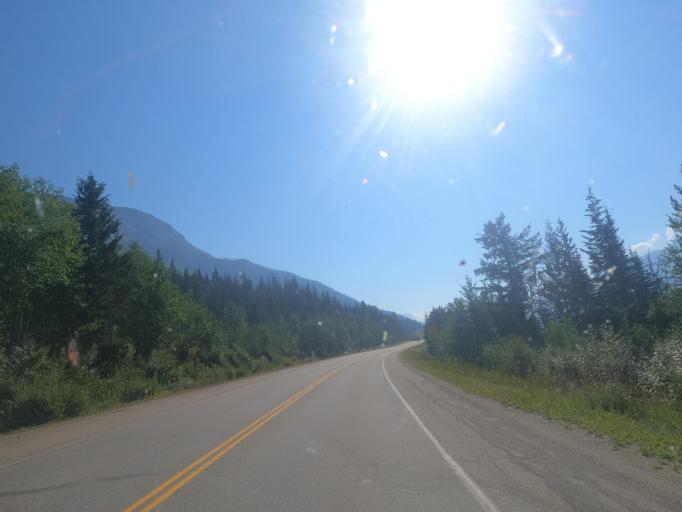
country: CA
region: Alberta
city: Jasper Park Lodge
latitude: 52.9719
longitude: -118.9398
